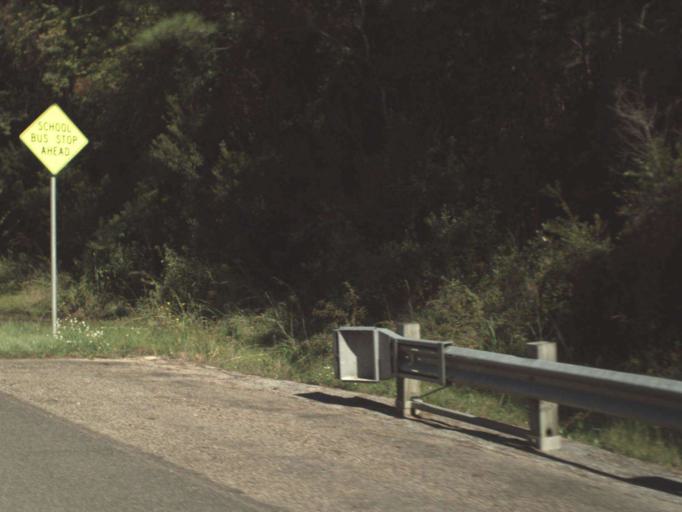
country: US
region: Florida
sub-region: Walton County
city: Freeport
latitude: 30.5783
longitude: -85.9298
